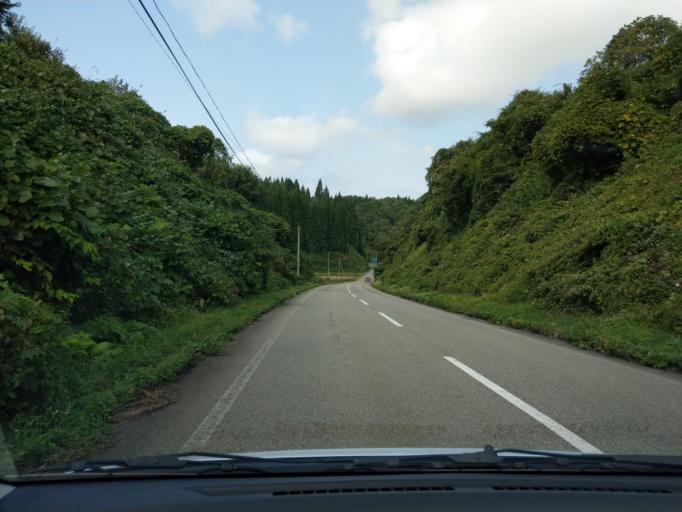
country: JP
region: Akita
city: Omagari
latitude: 39.4950
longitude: 140.3107
